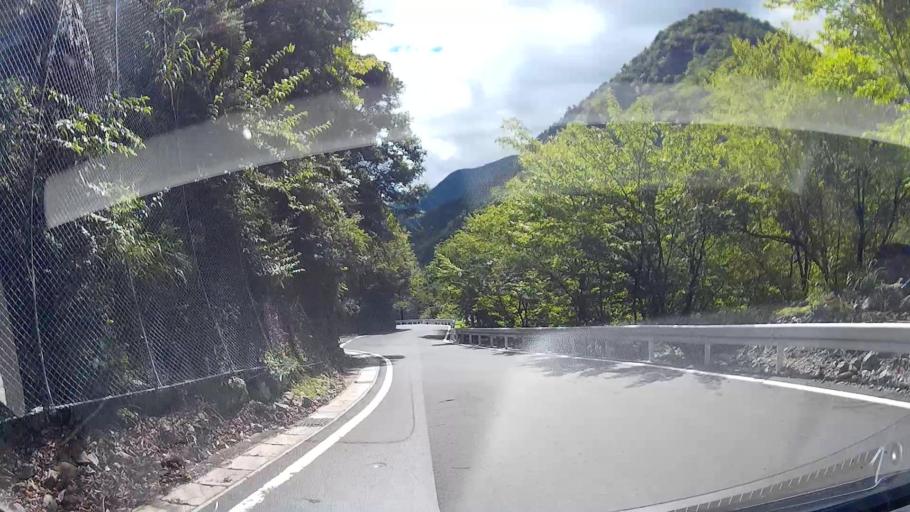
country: JP
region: Shizuoka
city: Shizuoka-shi
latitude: 35.3021
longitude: 138.2078
